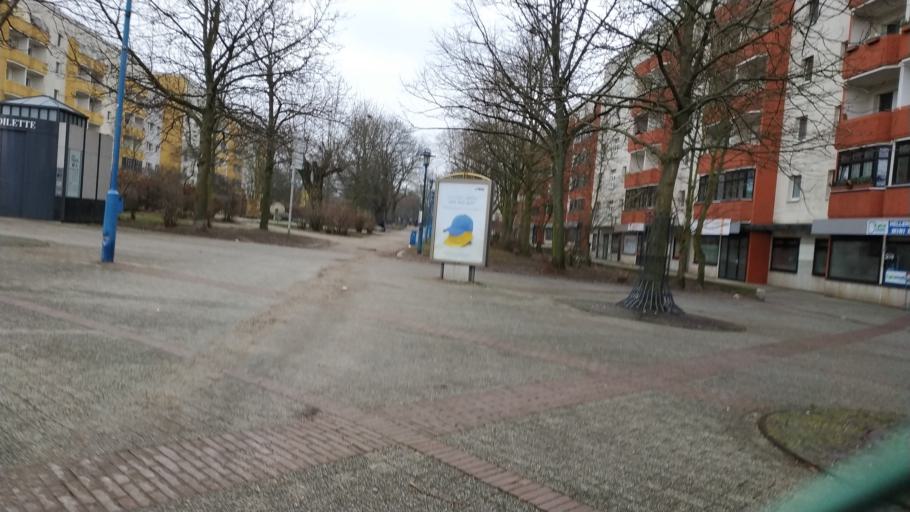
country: DE
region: Berlin
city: Hellersdorf
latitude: 52.5321
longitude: 13.6031
